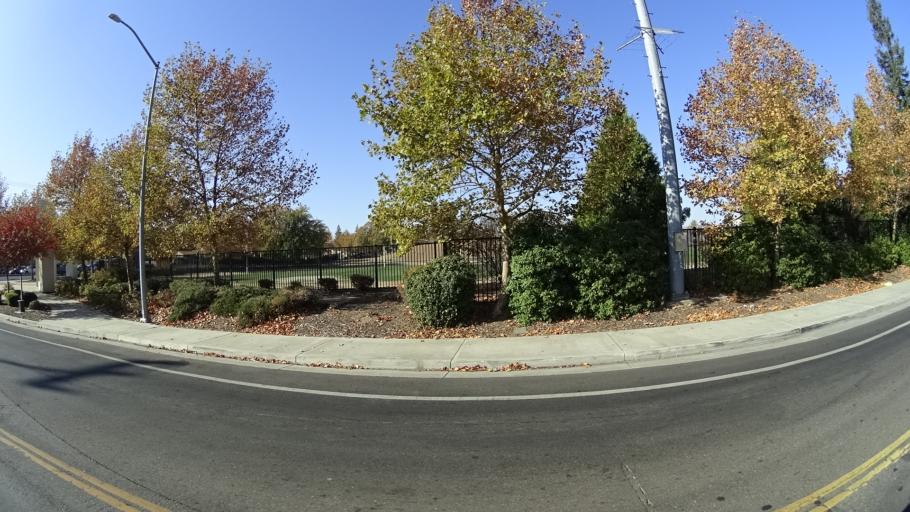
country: US
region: California
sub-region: Sacramento County
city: Citrus Heights
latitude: 38.6787
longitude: -121.2847
